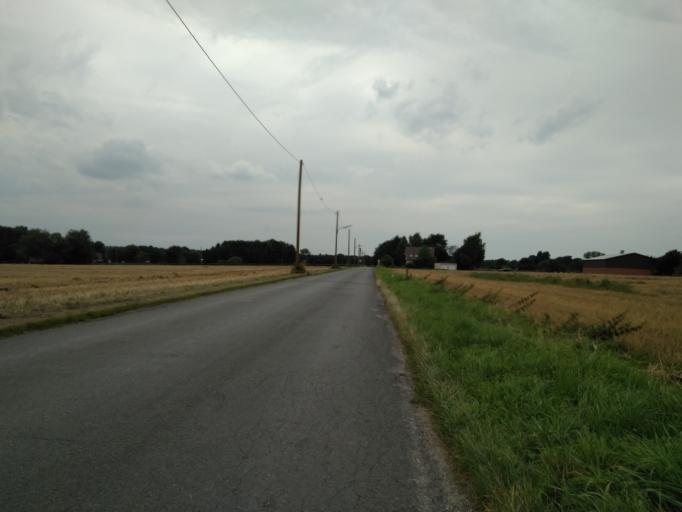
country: DE
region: North Rhine-Westphalia
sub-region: Regierungsbezirk Munster
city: Bottrop
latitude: 51.5990
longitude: 6.9038
